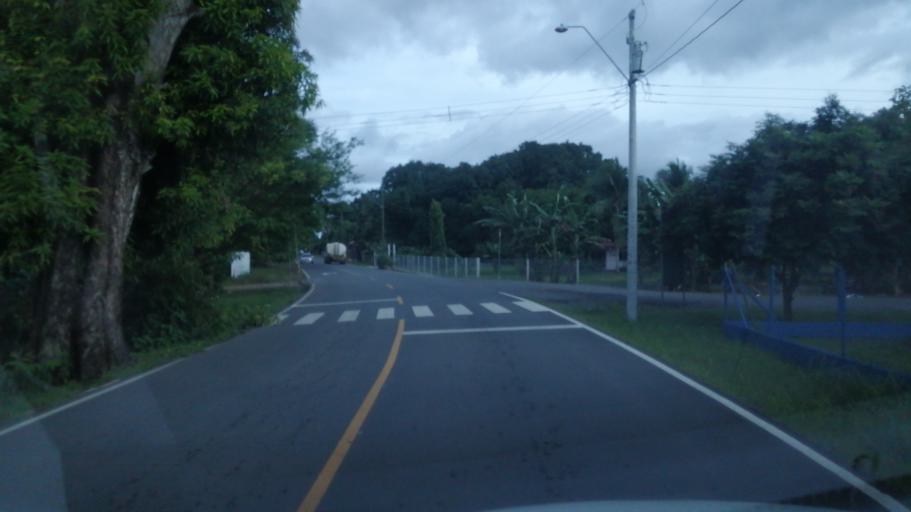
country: PA
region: Chiriqui
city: Alanje
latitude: 8.4180
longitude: -82.5199
